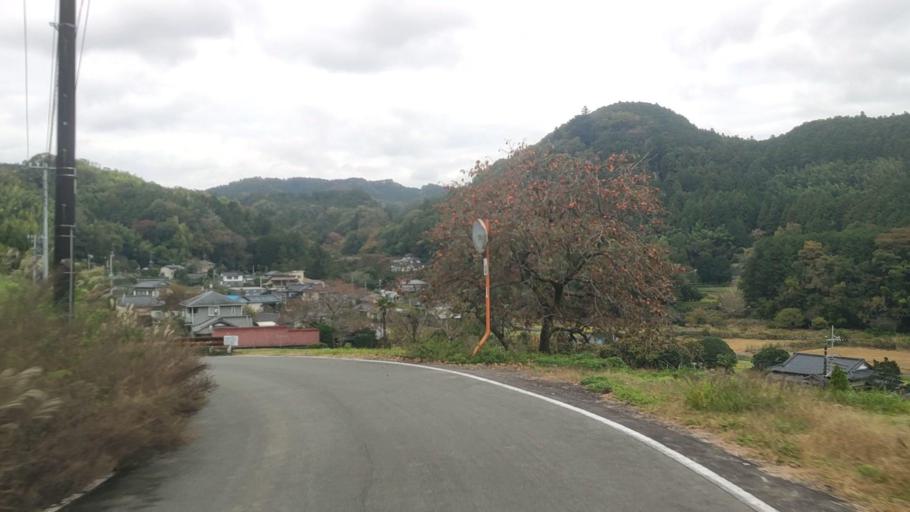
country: JP
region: Shizuoka
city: Ito
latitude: 34.9130
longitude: 138.9780
